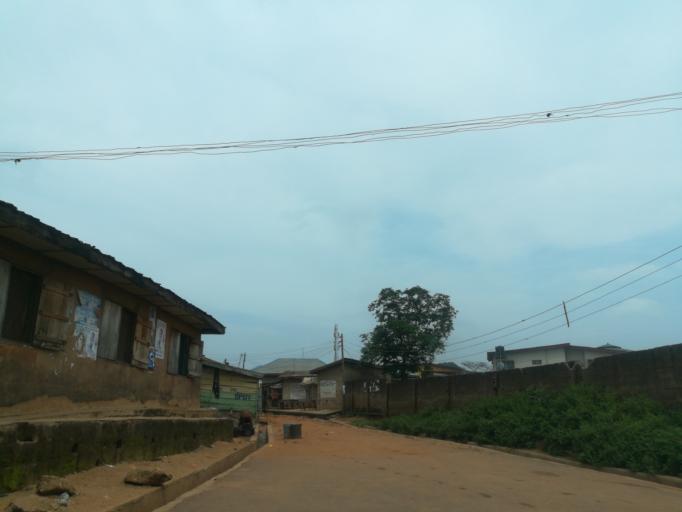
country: NG
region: Oyo
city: Ibadan
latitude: 7.4306
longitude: 3.9198
